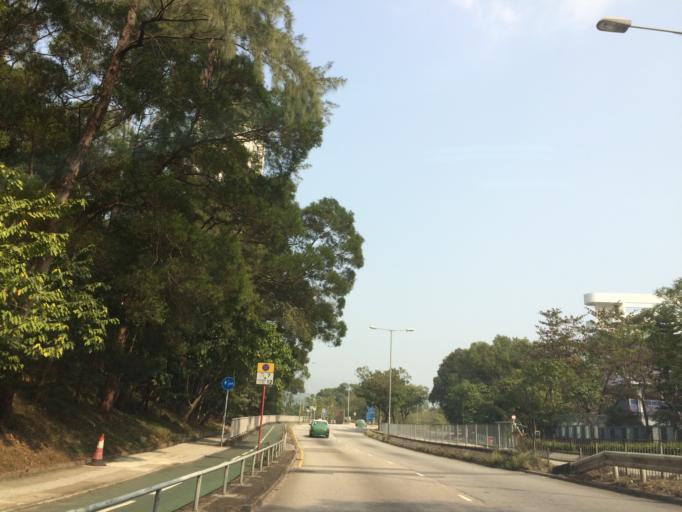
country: HK
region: Tai Po
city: Tai Po
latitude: 22.4558
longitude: 114.1753
